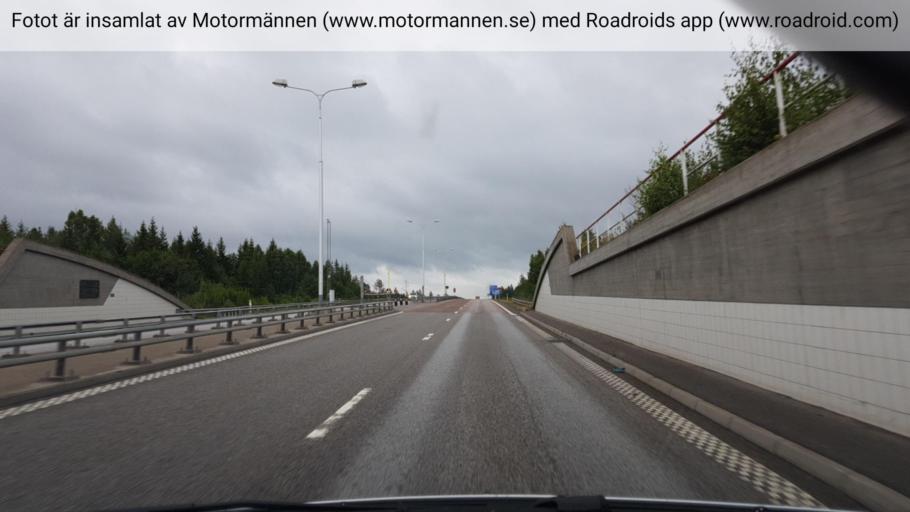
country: SE
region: Vaestra Goetaland
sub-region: Skovde Kommun
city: Skultorp
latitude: 58.3523
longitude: 13.8640
